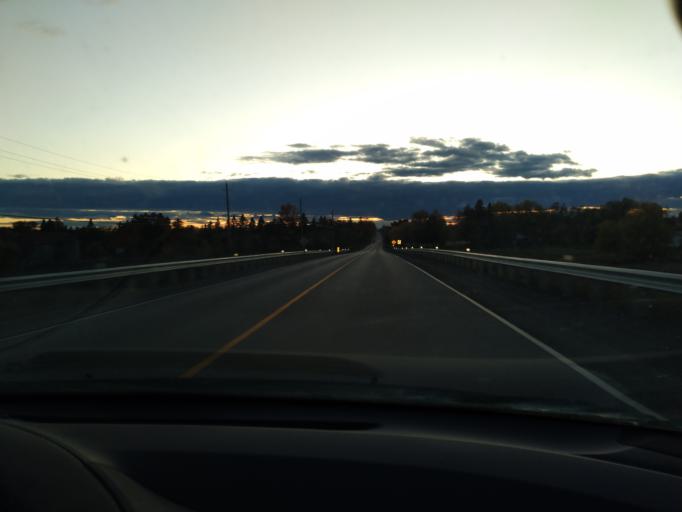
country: CA
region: Ontario
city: Innisfil
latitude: 44.2366
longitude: -79.6680
